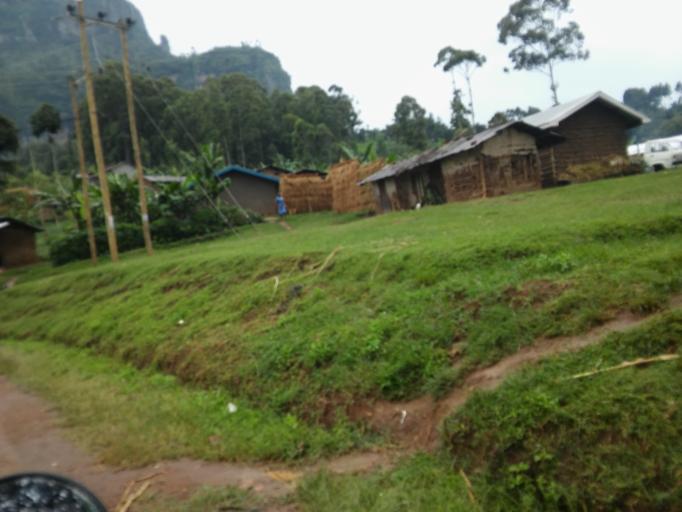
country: UG
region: Eastern Region
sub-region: Bududa District
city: Bududa
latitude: 1.0021
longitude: 34.2481
